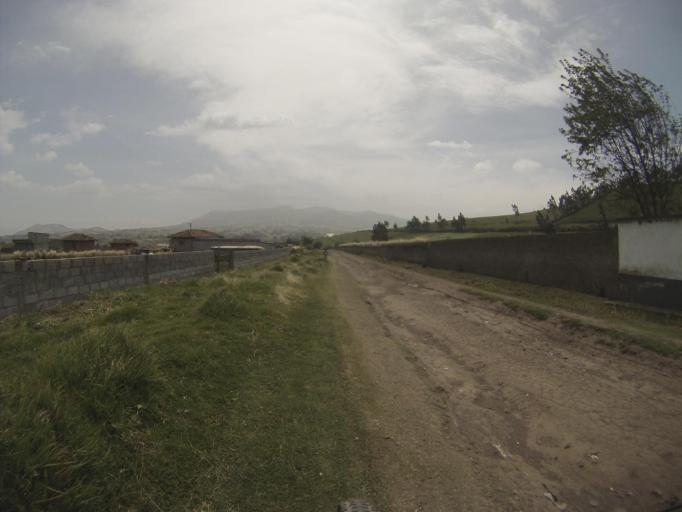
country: EC
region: Pichincha
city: Cayambe
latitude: 0.1587
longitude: -78.0689
